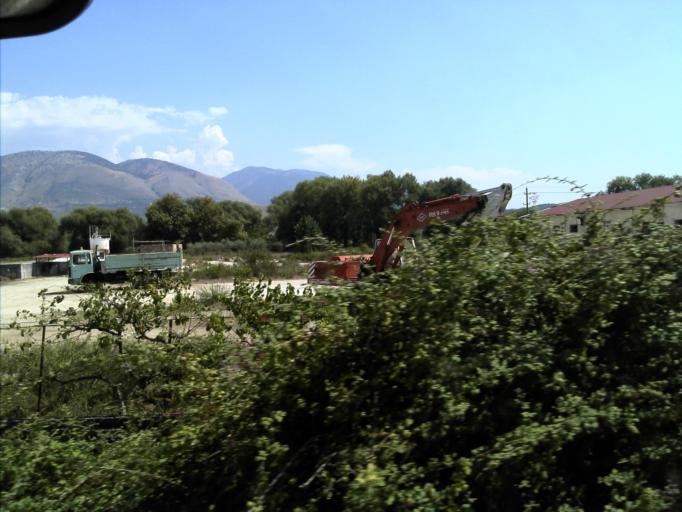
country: AL
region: Vlore
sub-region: Rrethi i Delvines
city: Mesopotam
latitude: 39.9081
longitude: 20.0889
